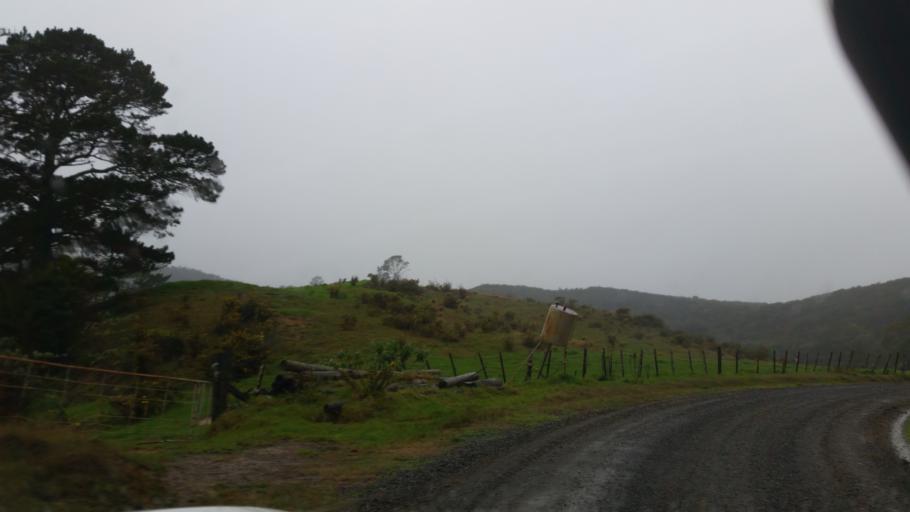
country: NZ
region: Northland
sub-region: Whangarei
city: Ngunguru
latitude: -35.5007
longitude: 174.4306
